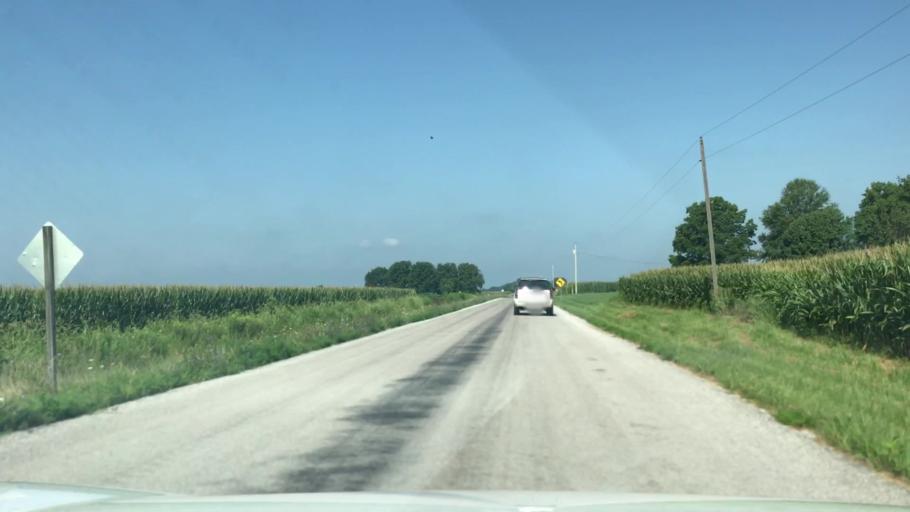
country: US
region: Illinois
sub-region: Washington County
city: Okawville
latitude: 38.4128
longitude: -89.4816
